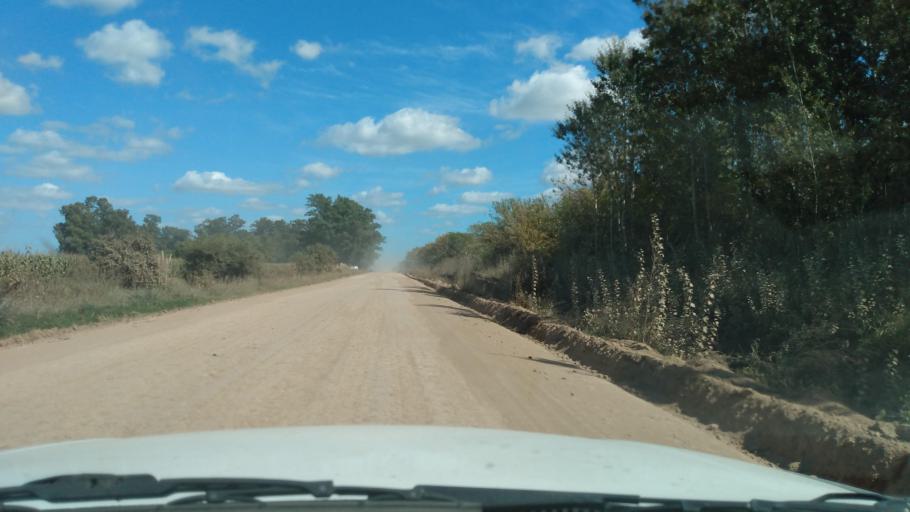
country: AR
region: Buenos Aires
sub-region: Partido de Navarro
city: Navarro
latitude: -35.0231
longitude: -59.4353
